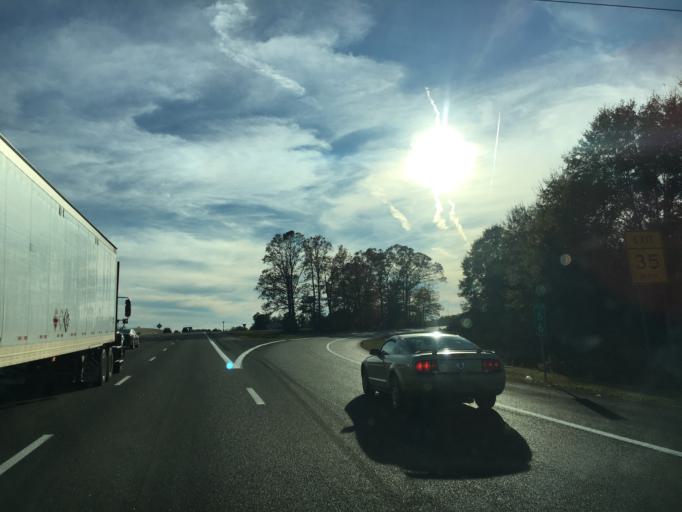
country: US
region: South Carolina
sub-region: Spartanburg County
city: Wellford
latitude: 34.9420
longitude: -82.0738
